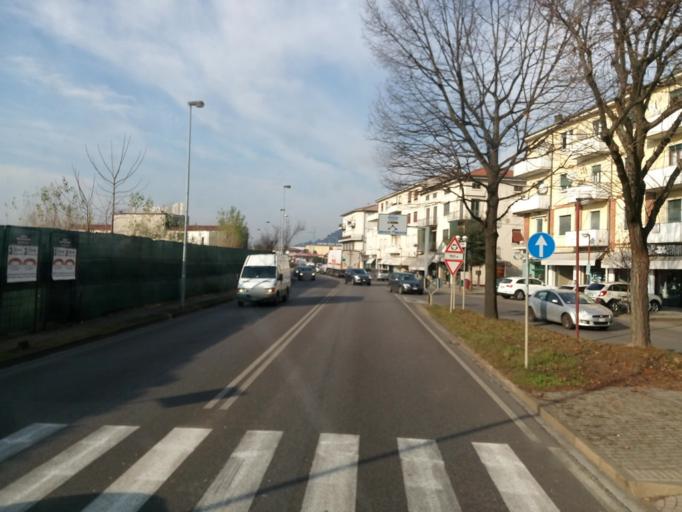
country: IT
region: Veneto
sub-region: Provincia di Vicenza
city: Brendola
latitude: 45.4935
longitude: 11.4329
